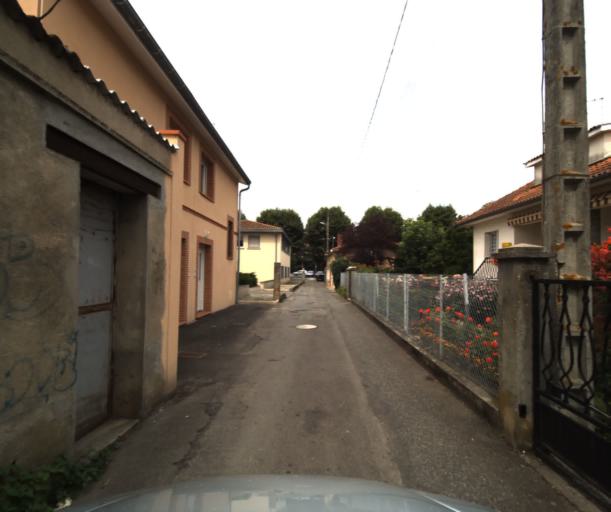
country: FR
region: Midi-Pyrenees
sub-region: Departement de la Haute-Garonne
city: Muret
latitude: 43.4635
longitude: 1.3249
